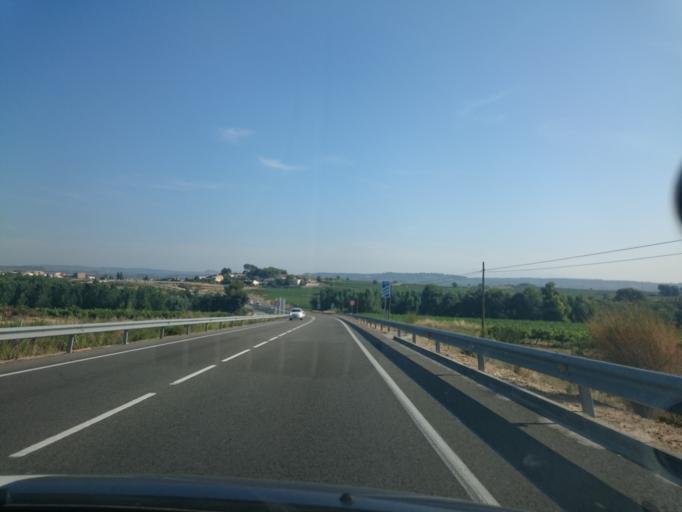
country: ES
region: Catalonia
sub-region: Provincia de Barcelona
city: La Granada
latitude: 41.3929
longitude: 1.7091
